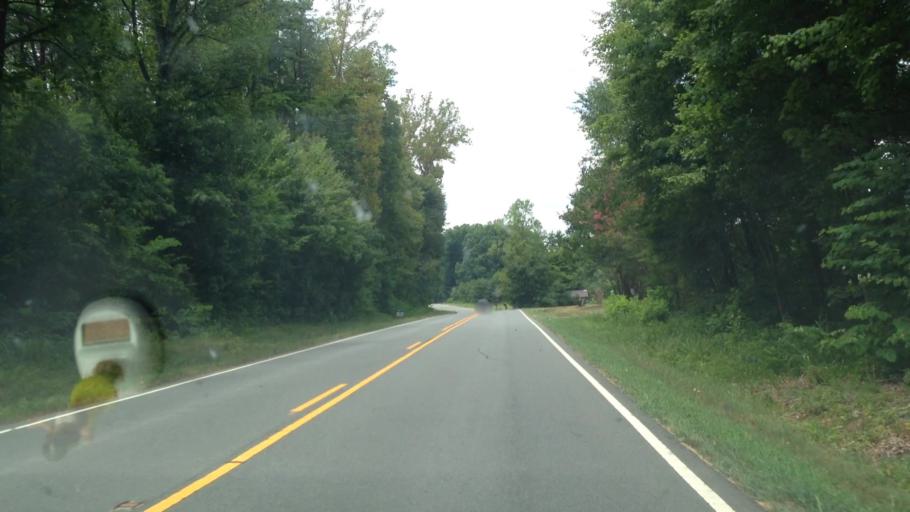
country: US
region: North Carolina
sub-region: Stokes County
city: Walnut Cove
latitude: 36.3780
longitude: -80.0908
